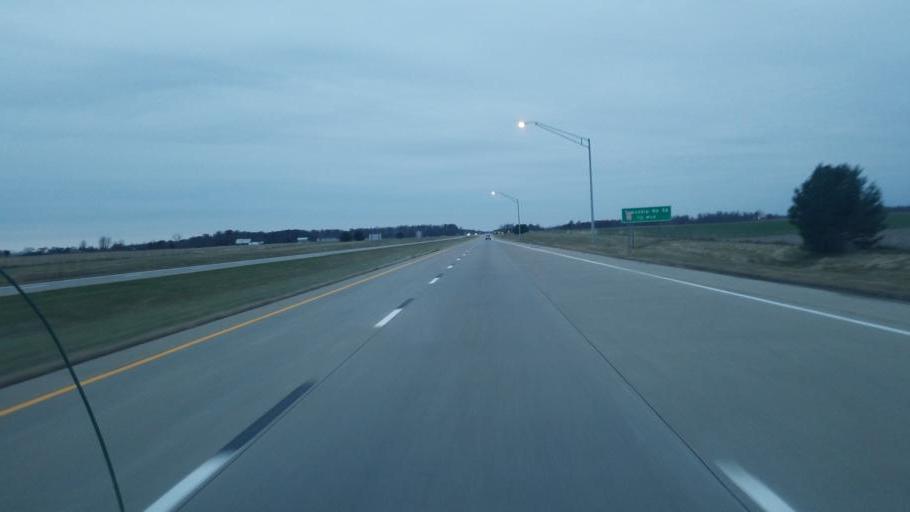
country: US
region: Ohio
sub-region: Hardin County
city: Ada
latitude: 40.8276
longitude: -83.8324
